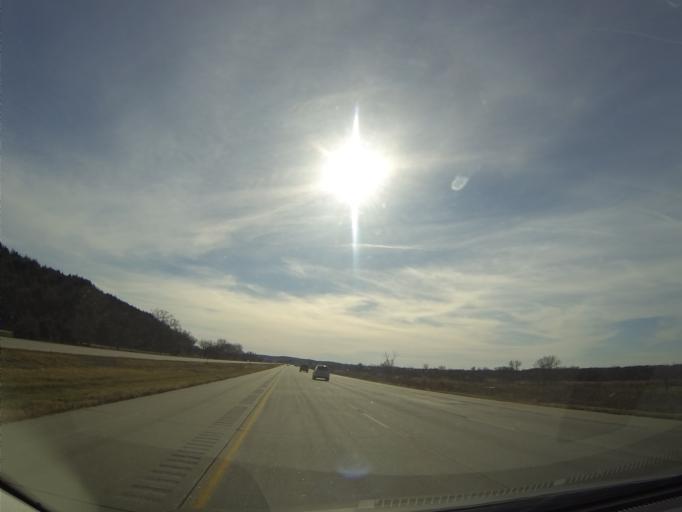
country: US
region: Nebraska
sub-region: Saunders County
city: Ashland
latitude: 41.0472
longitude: -96.2954
